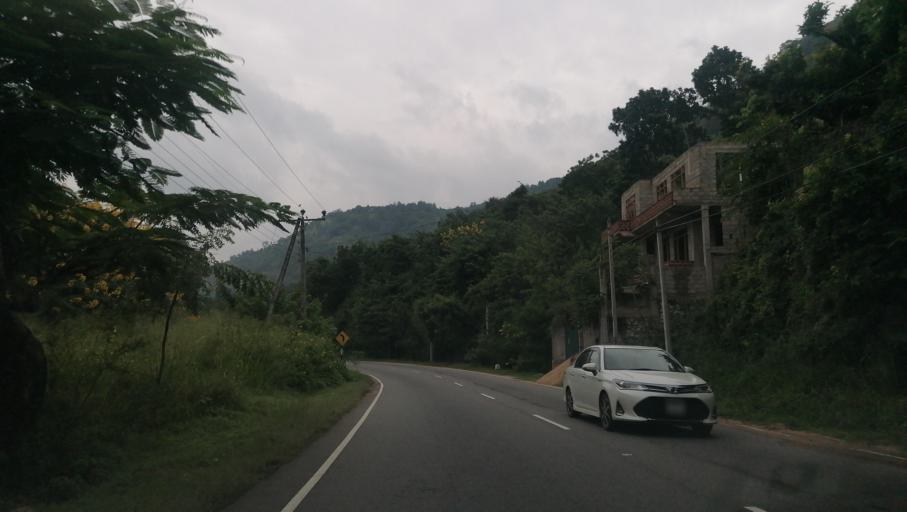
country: LK
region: Central
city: Kandy
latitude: 7.2466
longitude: 80.7259
